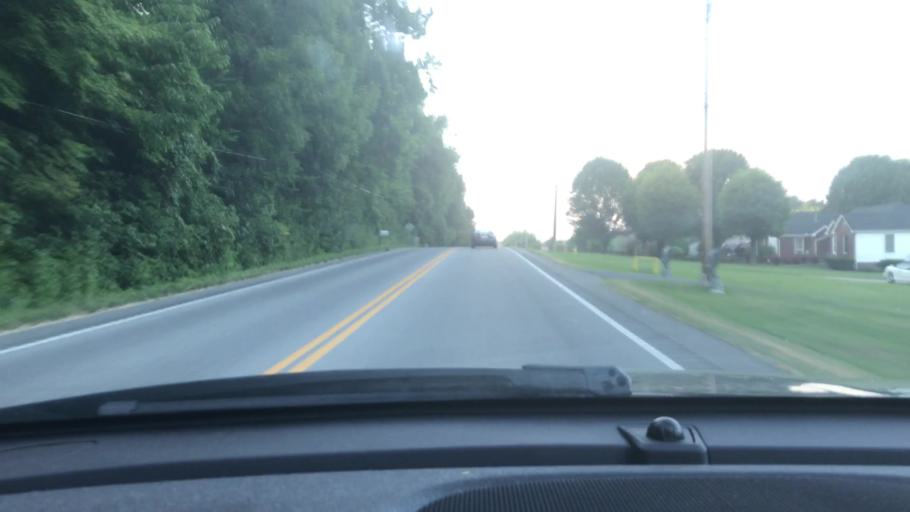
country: US
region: Tennessee
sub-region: Dickson County
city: Dickson
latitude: 36.1233
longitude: -87.3606
